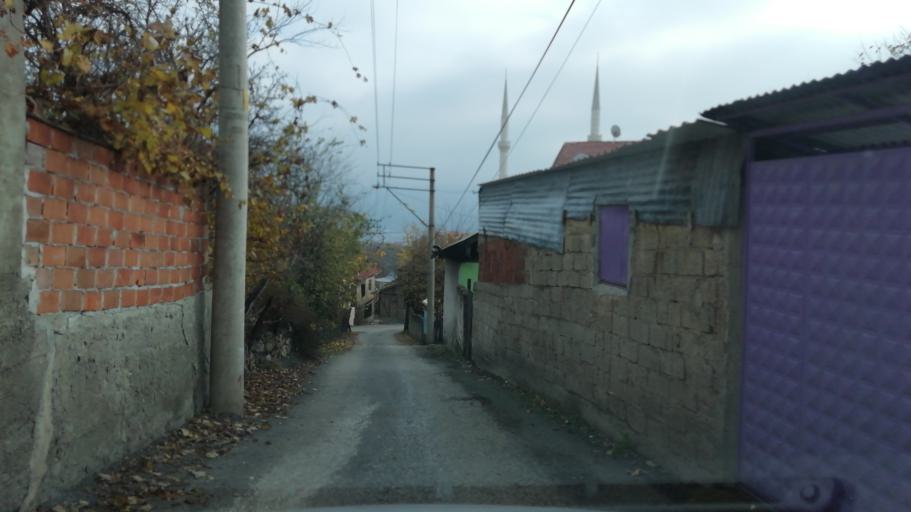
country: TR
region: Karabuk
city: Karabuk
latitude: 41.2274
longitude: 32.6210
